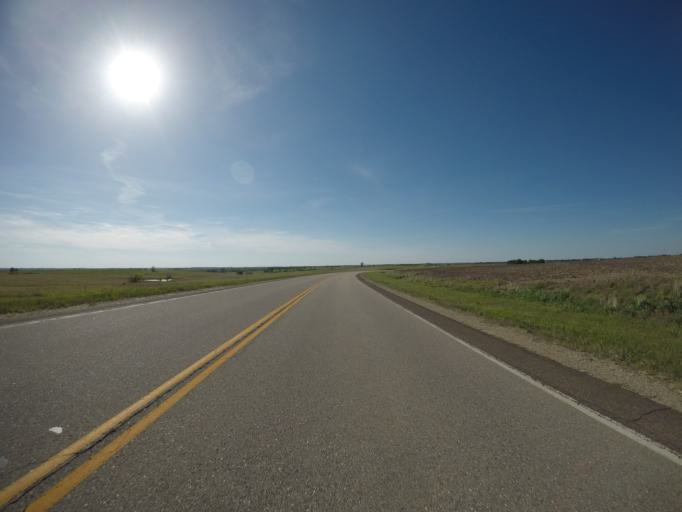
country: US
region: Kansas
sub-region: Clay County
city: Clay Center
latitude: 39.3660
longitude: -96.9467
